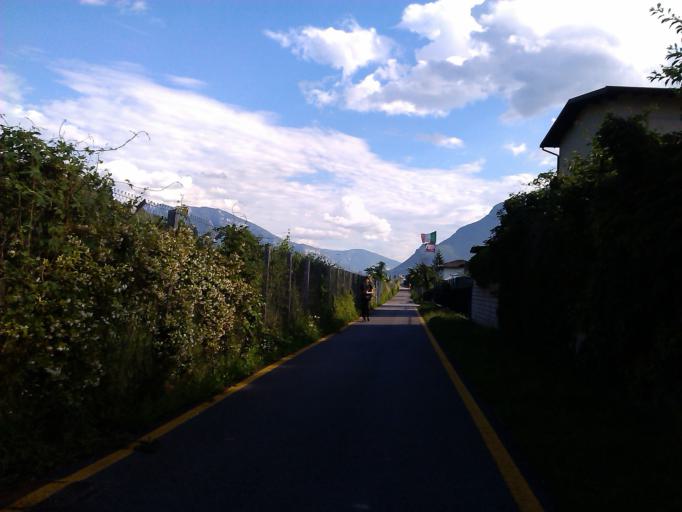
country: IT
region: Trentino-Alto Adige
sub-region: Provincia di Trento
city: Meano
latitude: 46.1190
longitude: 11.1081
